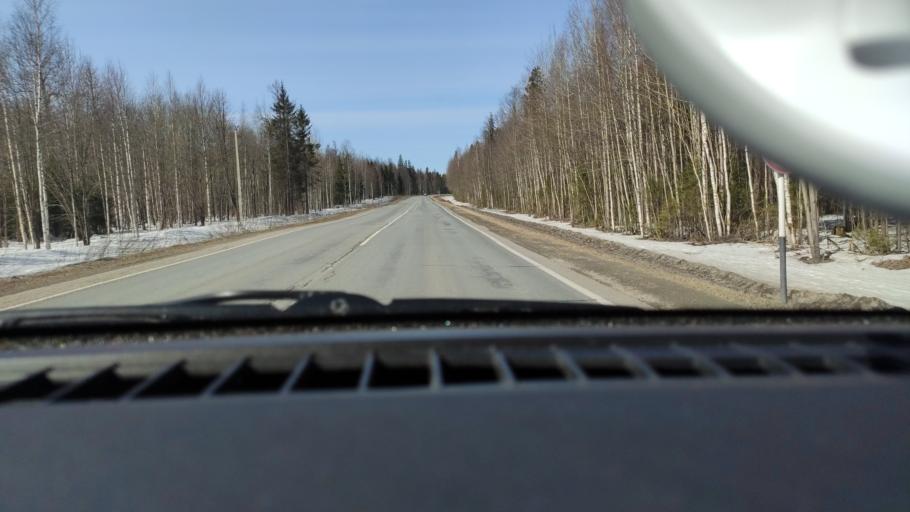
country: RU
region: Perm
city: Perm
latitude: 58.2119
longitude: 56.1838
